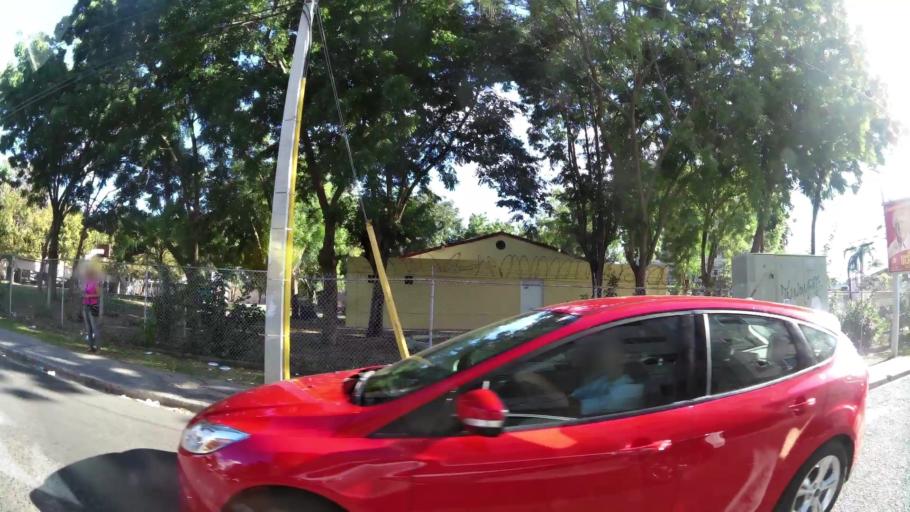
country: DO
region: Santiago
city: Santiago de los Caballeros
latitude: 19.4648
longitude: -70.6887
